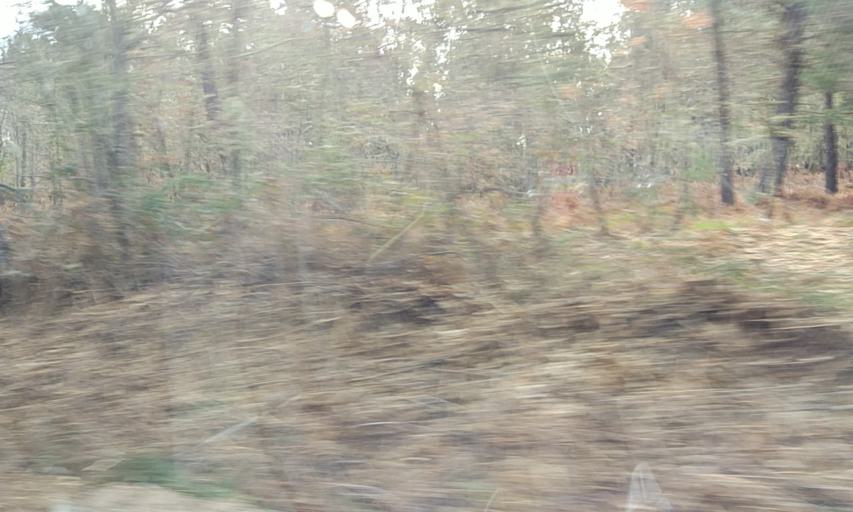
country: ES
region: Castille and Leon
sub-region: Provincia de Salamanca
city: Penaparda
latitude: 40.3042
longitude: -6.6528
